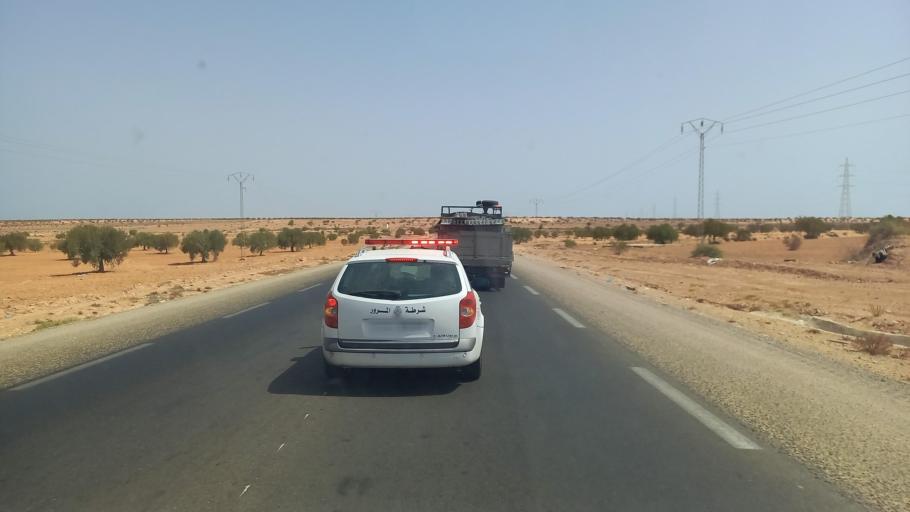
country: TN
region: Madanin
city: Zarzis
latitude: 33.4081
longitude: 10.8615
